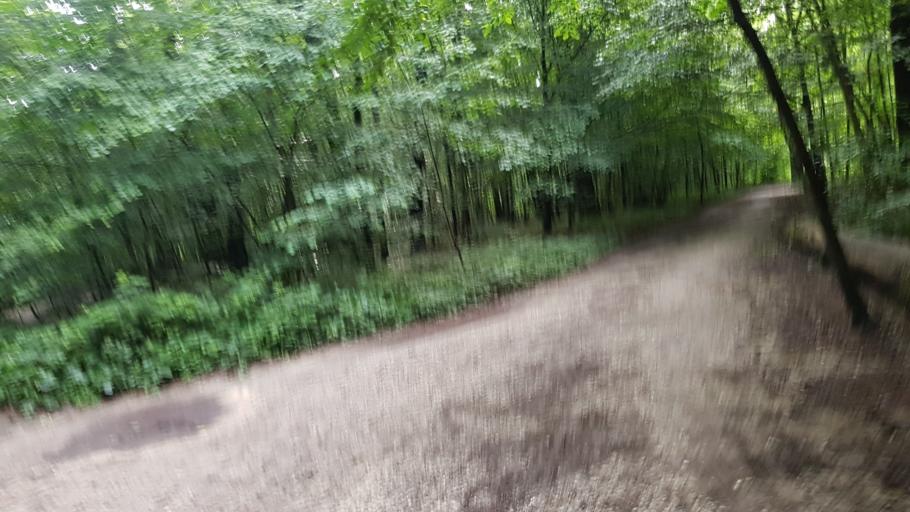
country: DE
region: Bavaria
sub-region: Upper Bavaria
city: Pasing
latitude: 48.1684
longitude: 11.4956
